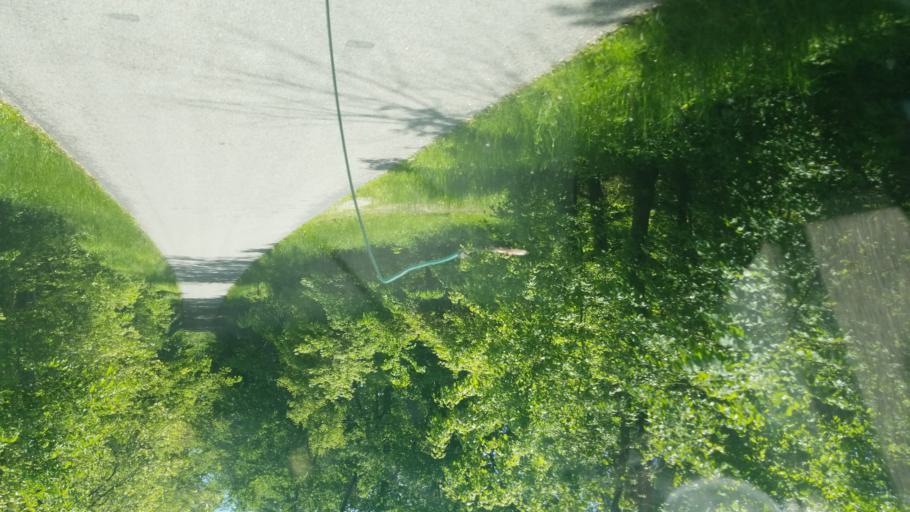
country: US
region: Ohio
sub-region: Huron County
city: Willard
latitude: 41.1203
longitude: -82.7155
